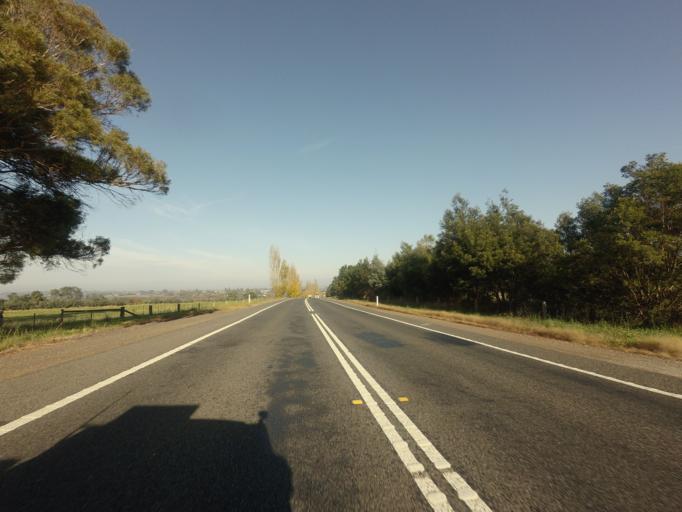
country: AU
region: Tasmania
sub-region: Northern Midlands
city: Longford
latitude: -41.5816
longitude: 147.1340
